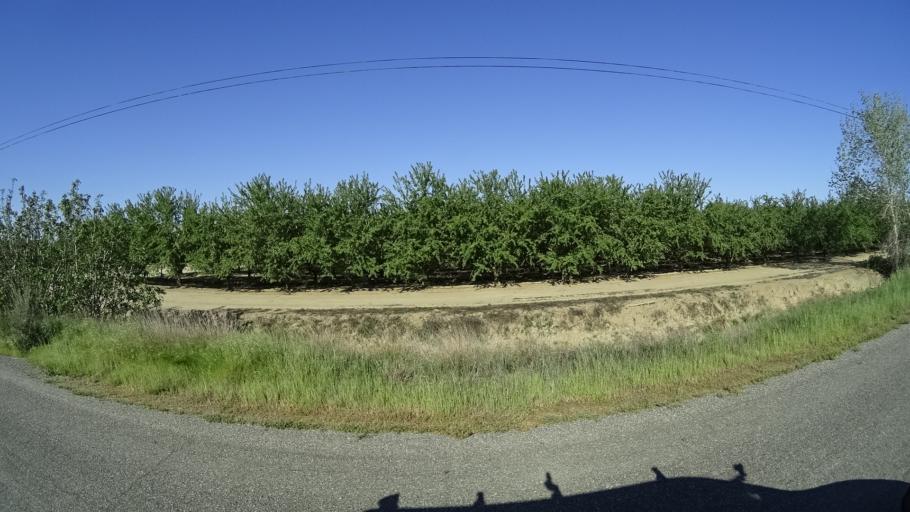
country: US
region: California
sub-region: Glenn County
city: Hamilton City
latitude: 39.7027
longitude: -122.0548
